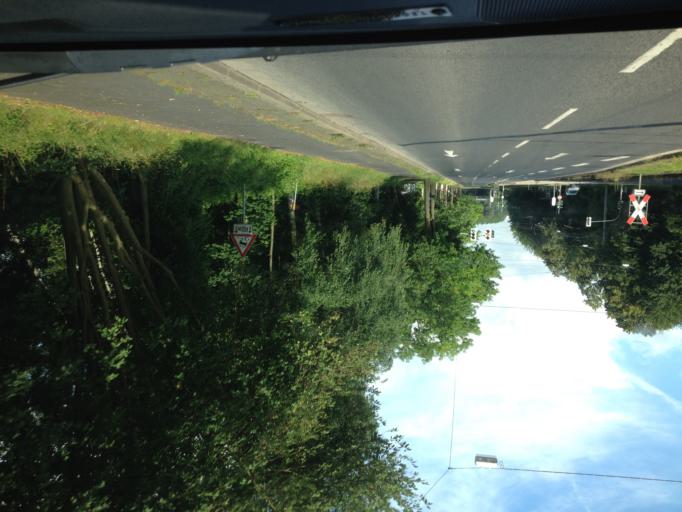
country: DE
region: North Rhine-Westphalia
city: Witten
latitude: 51.4661
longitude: 7.2945
